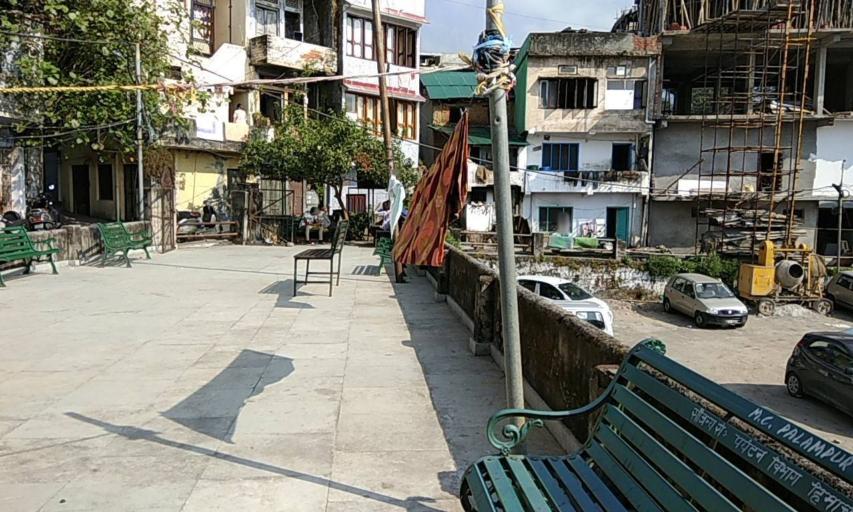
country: IN
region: Himachal Pradesh
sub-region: Kangra
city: Palampur
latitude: 32.1091
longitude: 76.5362
